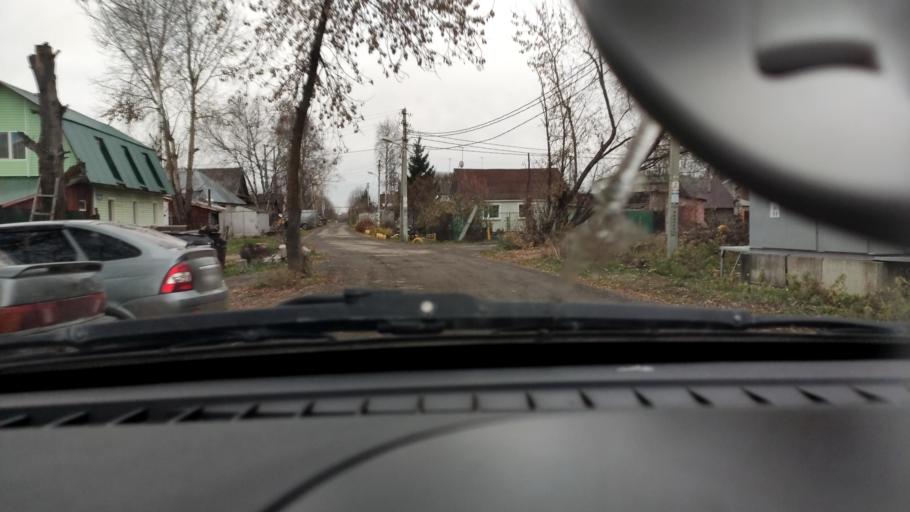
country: RU
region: Perm
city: Kondratovo
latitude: 57.9985
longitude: 56.1201
